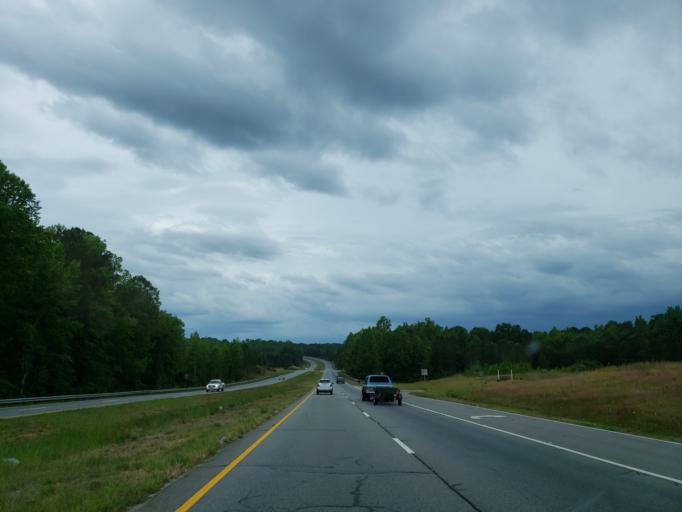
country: US
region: Georgia
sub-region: Haralson County
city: Bremen
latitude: 33.7053
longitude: -85.1597
